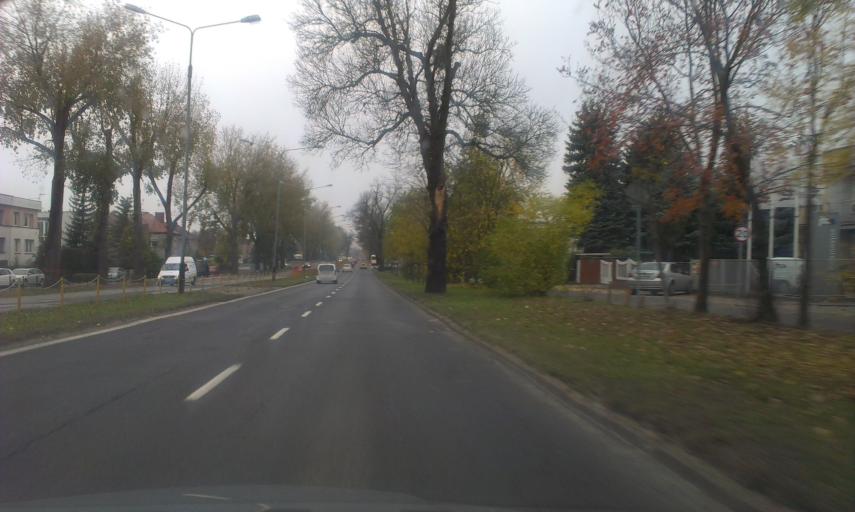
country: PL
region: Greater Poland Voivodeship
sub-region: Powiat poznanski
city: Suchy Las
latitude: 52.4268
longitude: 16.8575
